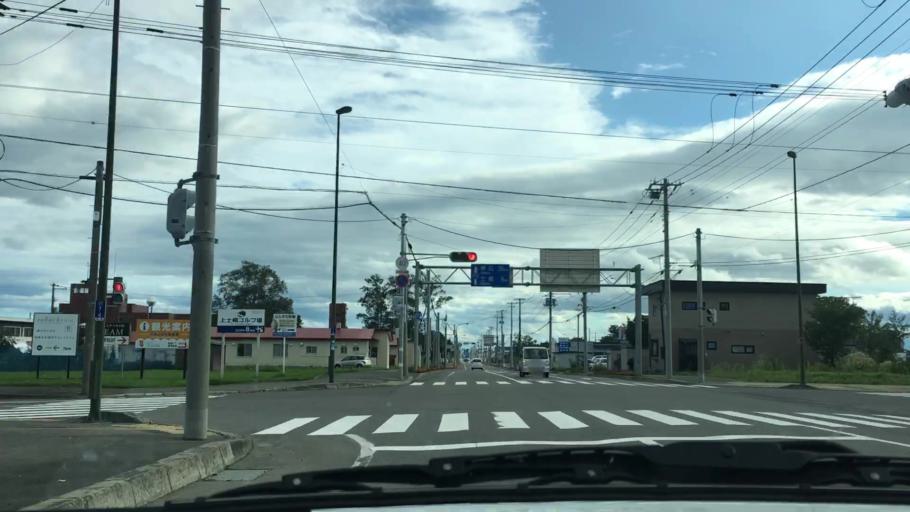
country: JP
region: Hokkaido
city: Otofuke
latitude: 43.2349
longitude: 143.2956
